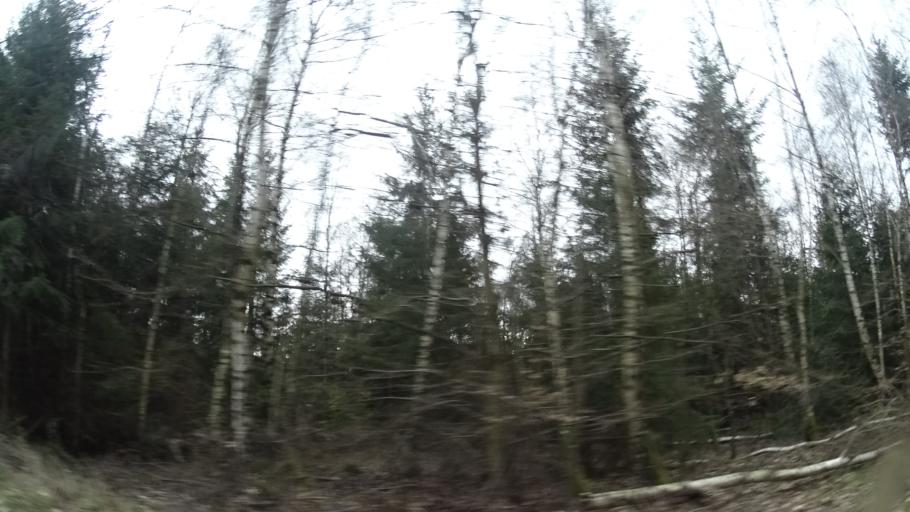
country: DE
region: Rheinland-Pfalz
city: Waldalgesheim
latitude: 49.9736
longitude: 7.8374
